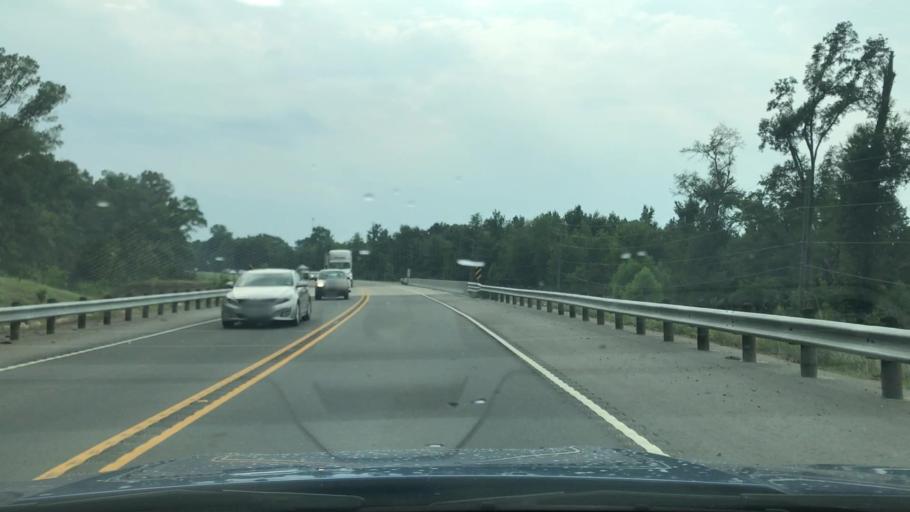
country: US
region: Louisiana
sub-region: Caddo Parish
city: Greenwood
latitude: 32.4566
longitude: -94.0147
